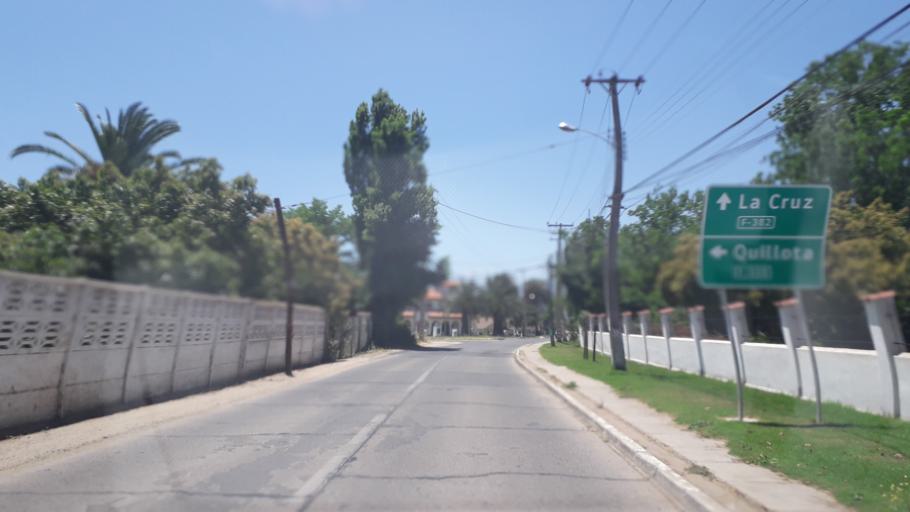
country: CL
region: Valparaiso
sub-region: Provincia de Quillota
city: Quillota
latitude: -32.9153
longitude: -71.2333
